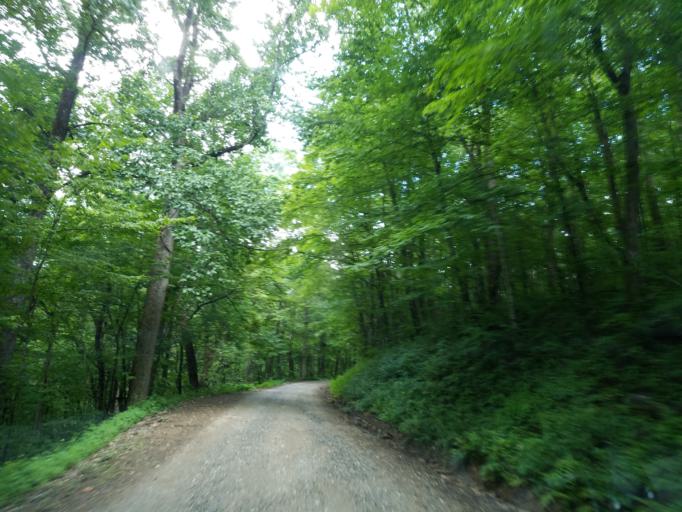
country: US
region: Georgia
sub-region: Dawson County
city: Dawsonville
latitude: 34.6433
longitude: -84.2032
